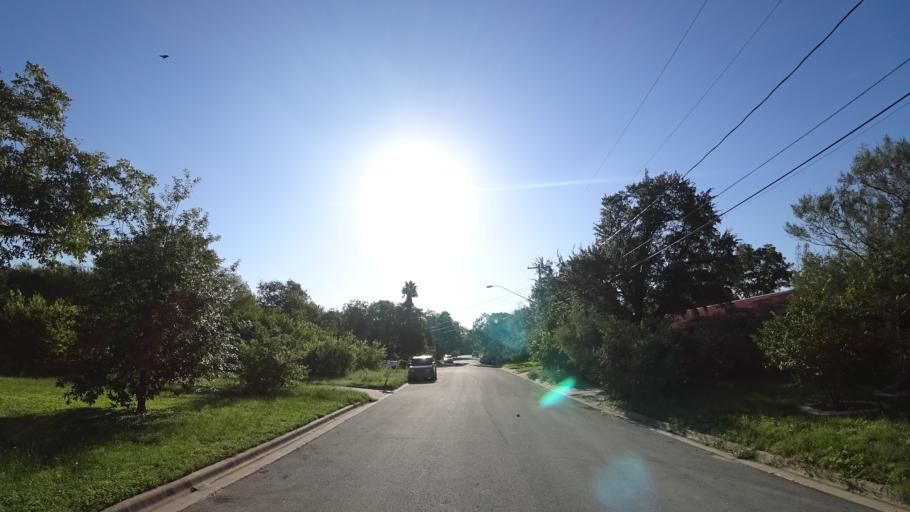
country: US
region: Texas
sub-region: Travis County
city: Austin
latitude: 30.3463
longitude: -97.7025
